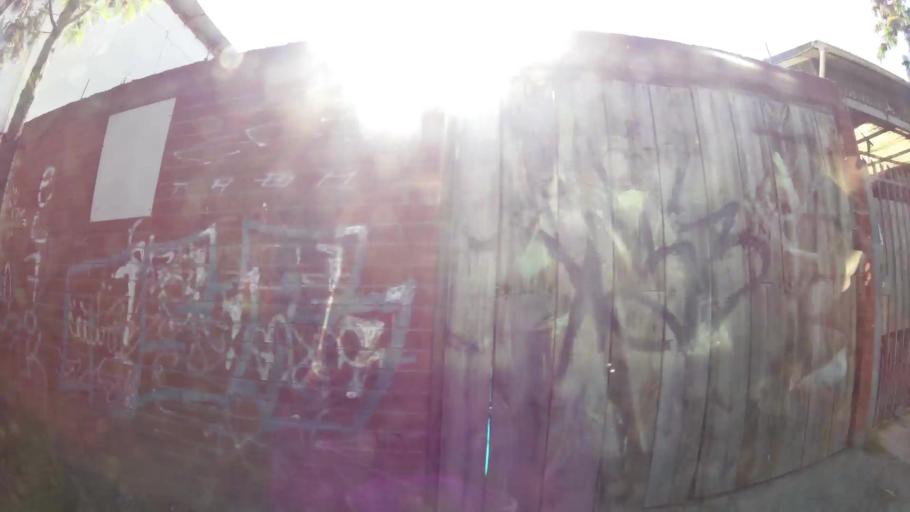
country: CL
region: Santiago Metropolitan
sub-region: Provincia de Maipo
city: San Bernardo
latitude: -33.5650
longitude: -70.7027
